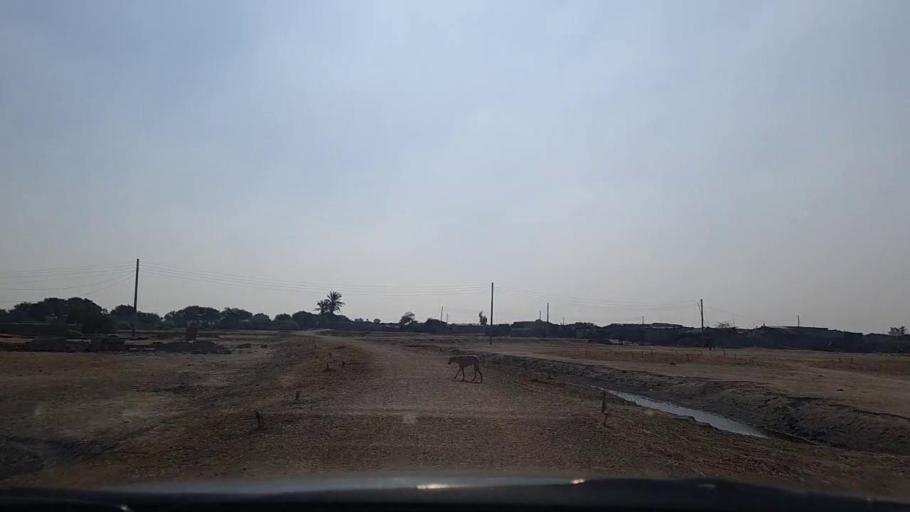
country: PK
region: Sindh
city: Mirpur Sakro
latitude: 24.5509
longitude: 67.6990
